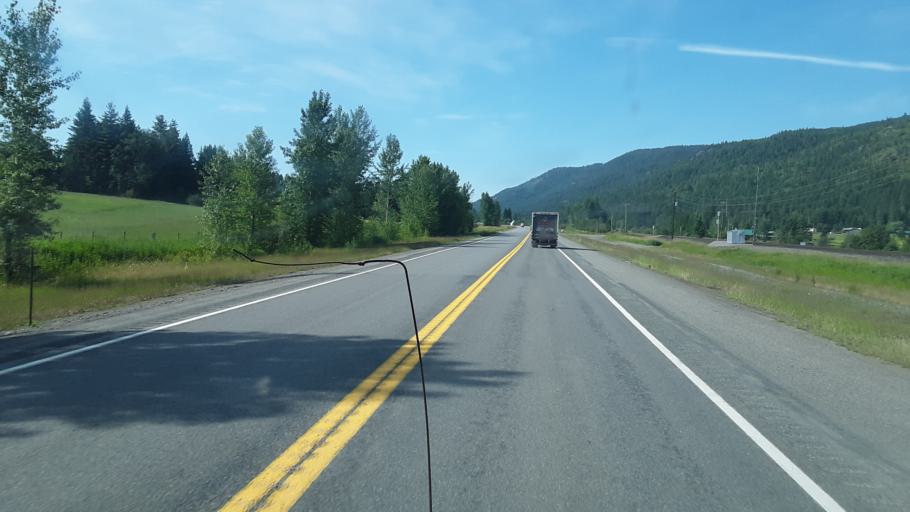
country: US
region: Idaho
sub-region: Bonner County
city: Ponderay
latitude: 48.3881
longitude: -116.5409
